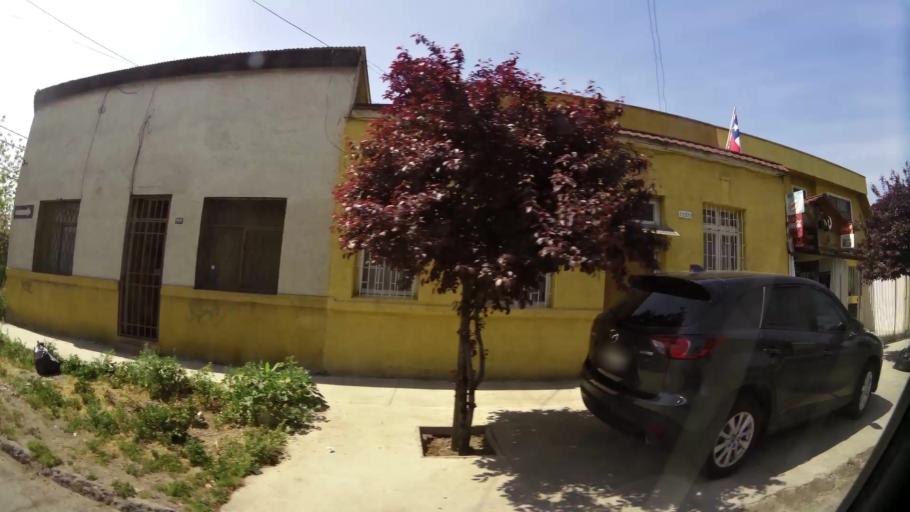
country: CL
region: Santiago Metropolitan
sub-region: Provincia de Santiago
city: Lo Prado
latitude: -33.4313
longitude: -70.6991
